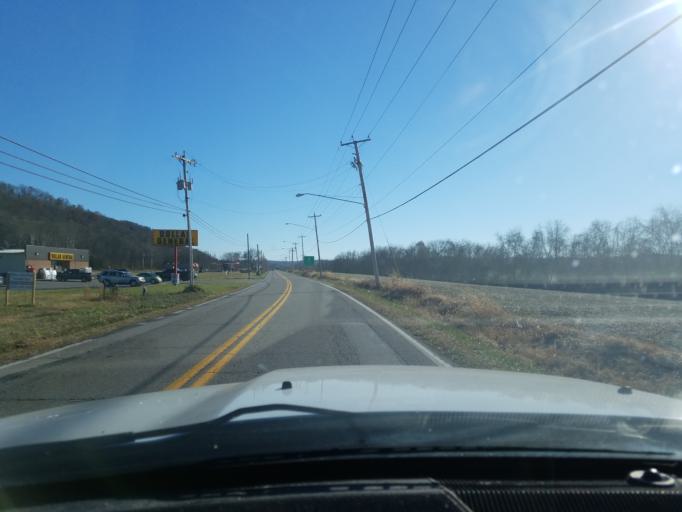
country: US
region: West Virginia
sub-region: Putnam County
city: Buffalo
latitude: 38.5886
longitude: -81.9963
